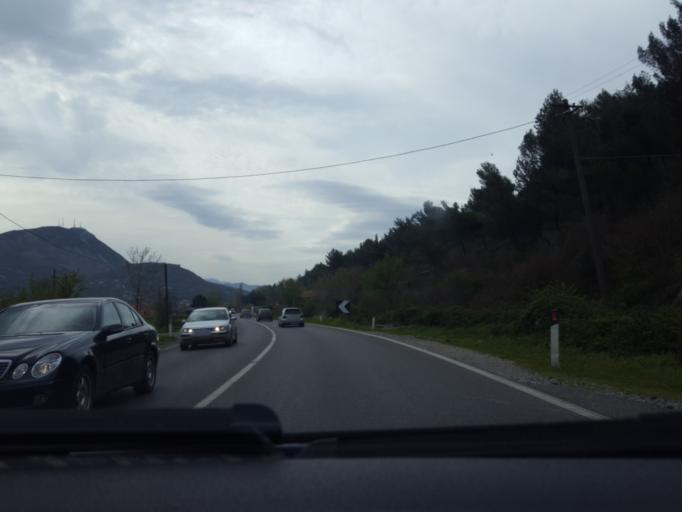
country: AL
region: Lezhe
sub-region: Rrethi i Lezhes
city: Balldreni i Ri
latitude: 41.8011
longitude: 19.6305
